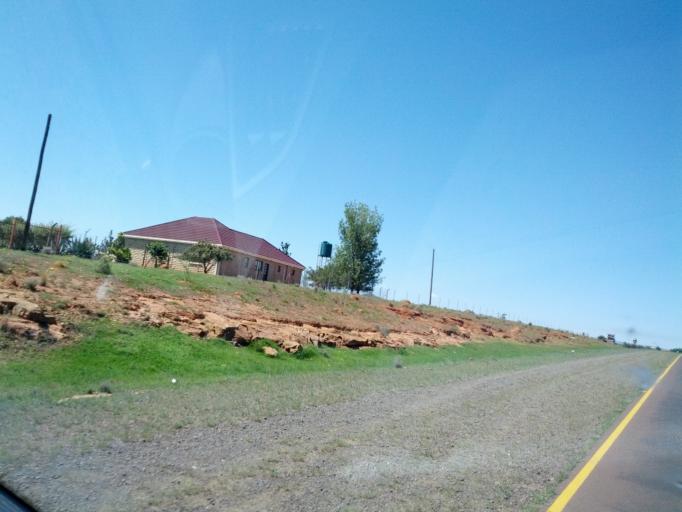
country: LS
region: Maseru
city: Maseru
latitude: -29.4435
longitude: 27.5619
